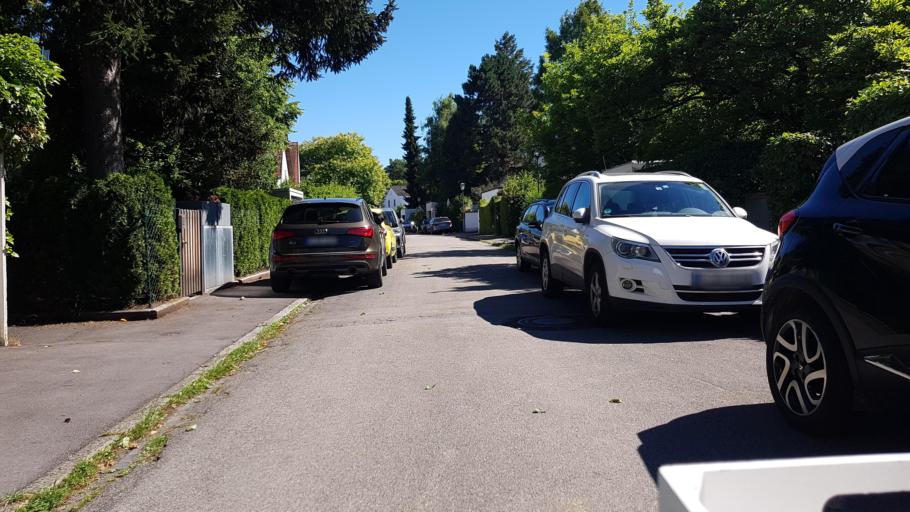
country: DE
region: Bavaria
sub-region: Upper Bavaria
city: Bogenhausen
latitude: 48.1135
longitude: 11.6094
